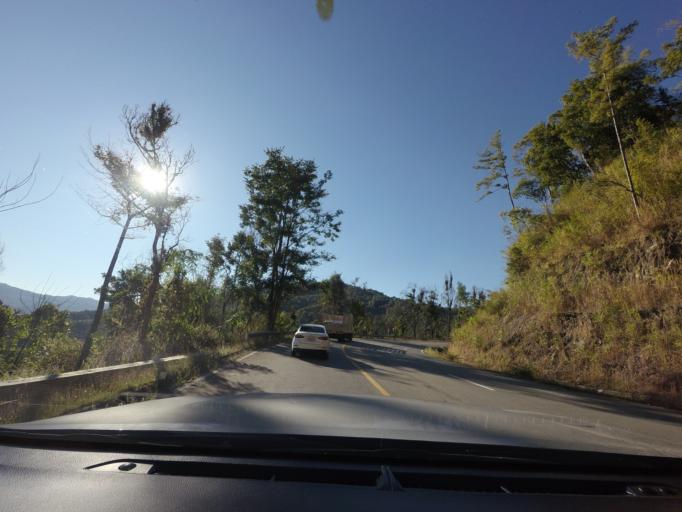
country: TH
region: Mae Hong Son
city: Mae Hi
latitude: 19.2295
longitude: 98.6717
